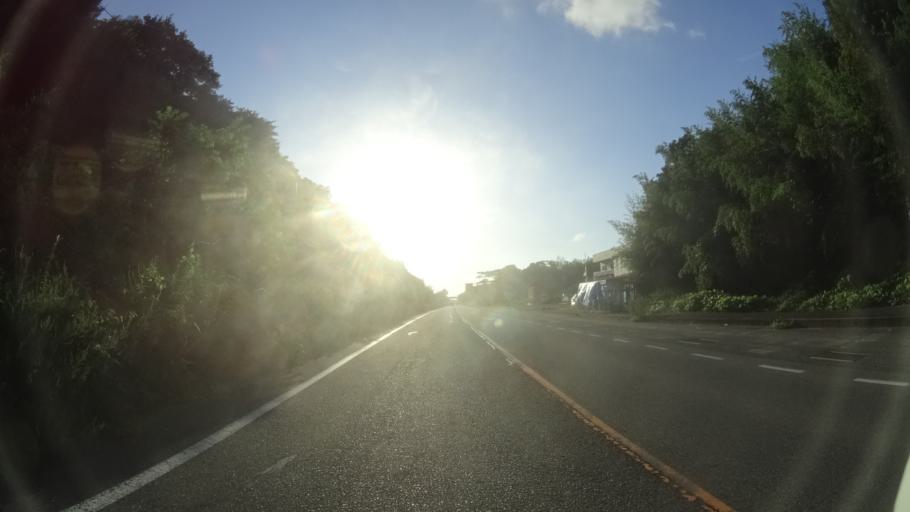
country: JP
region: Tottori
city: Yonago
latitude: 35.5134
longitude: 133.5349
